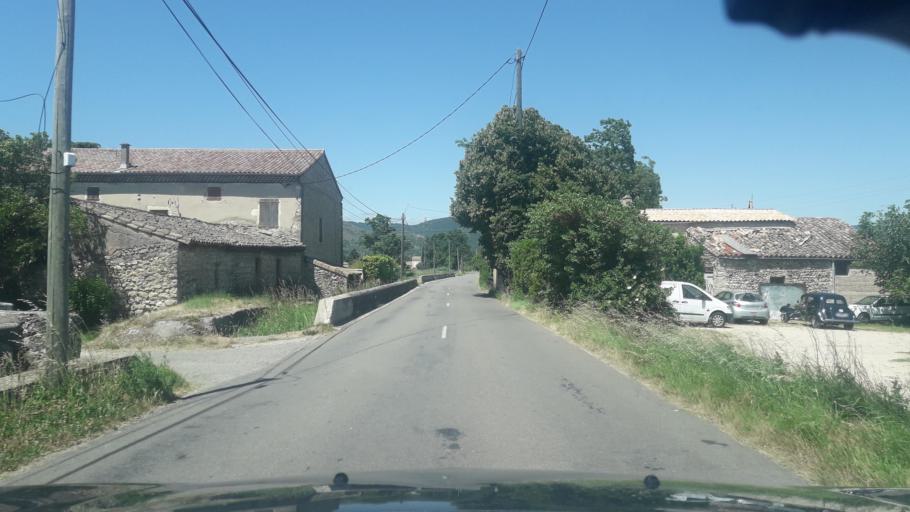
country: FR
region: Rhone-Alpes
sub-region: Departement de la Drome
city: Loriol-sur-Drome
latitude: 44.7863
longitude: 4.8112
